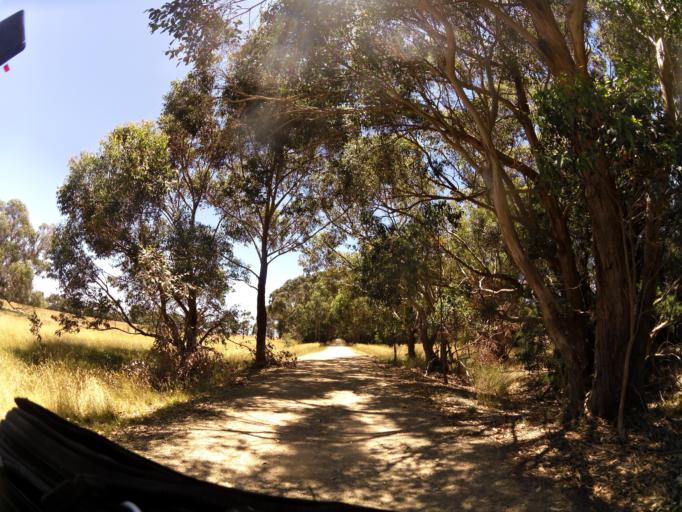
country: AU
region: Victoria
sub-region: Ballarat North
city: Delacombe
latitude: -37.5744
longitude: 143.7286
